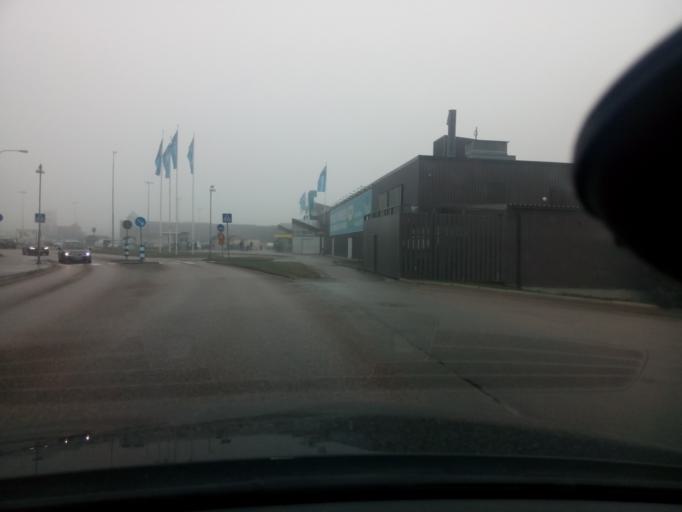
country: SE
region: Soedermanland
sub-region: Nykopings Kommun
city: Nykoping
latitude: 58.7688
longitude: 17.0248
